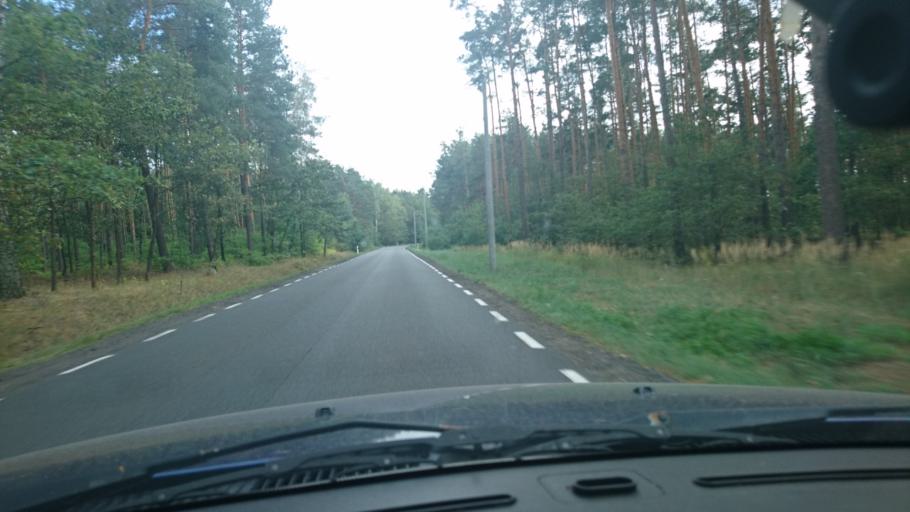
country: PL
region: Greater Poland Voivodeship
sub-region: Powiat ostrowski
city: Jankow Przygodzki
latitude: 51.5160
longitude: 17.7662
